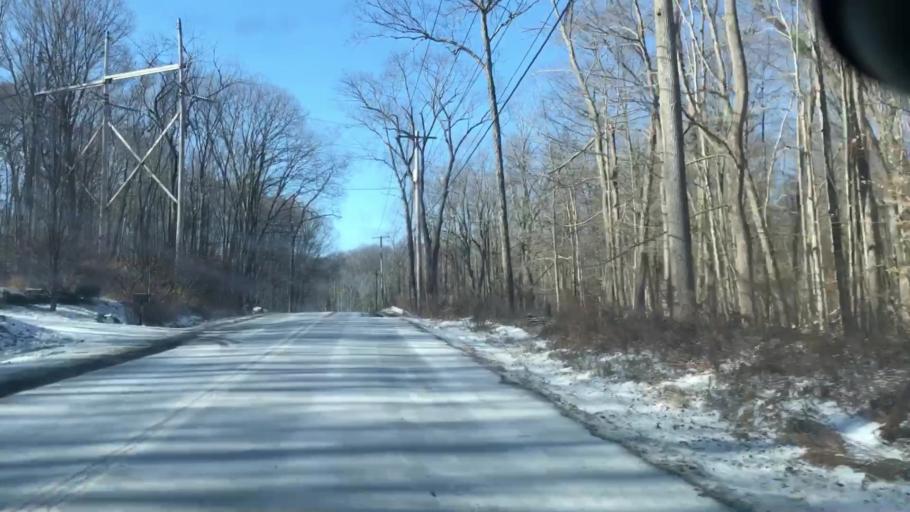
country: US
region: New York
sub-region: Putnam County
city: Carmel Hamlet
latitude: 41.3884
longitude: -73.6861
